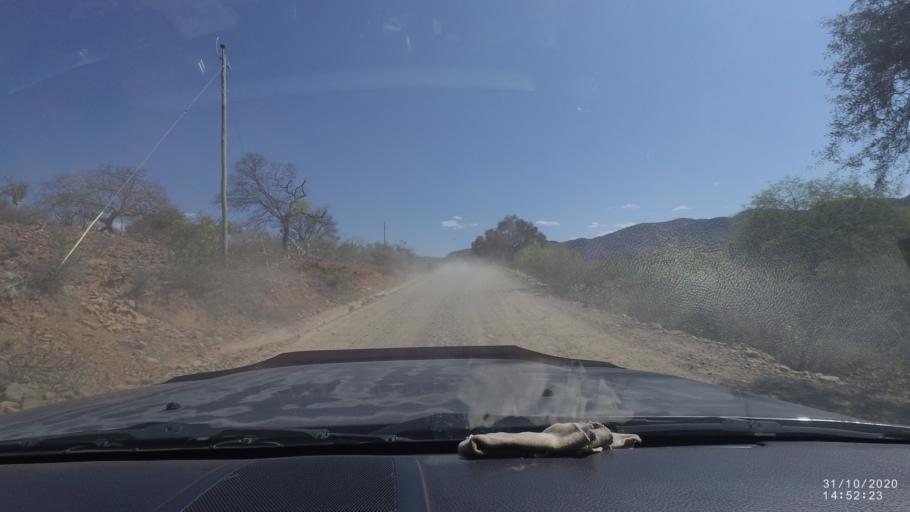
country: BO
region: Cochabamba
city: Aiquile
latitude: -18.2134
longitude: -64.8565
